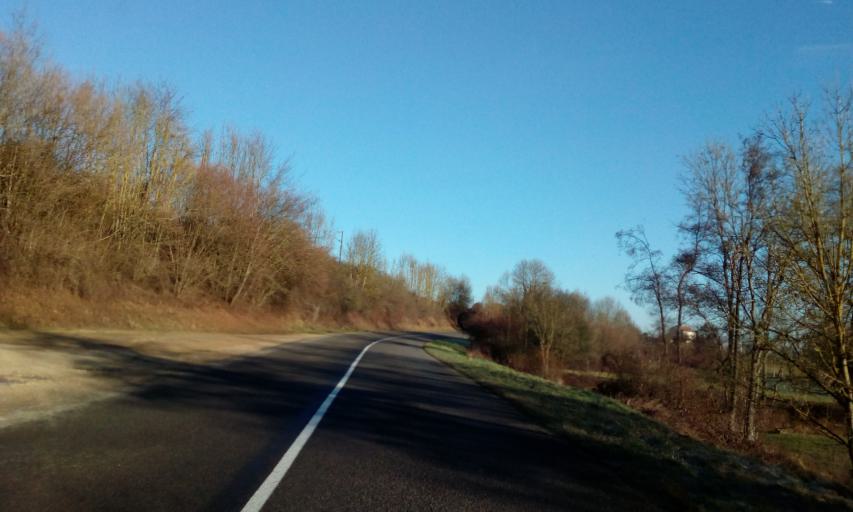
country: FR
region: Champagne-Ardenne
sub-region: Departement des Ardennes
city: Rimogne
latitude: 49.7780
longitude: 4.4592
